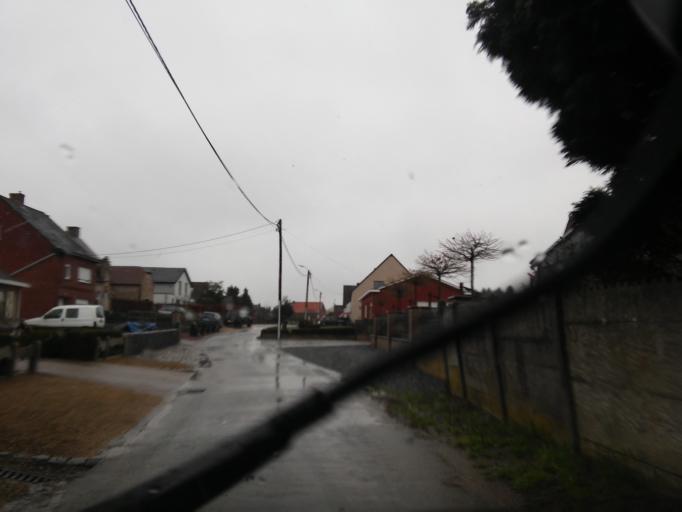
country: BE
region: Flanders
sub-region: Provincie Antwerpen
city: Hulshout
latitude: 51.0699
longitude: 4.8113
